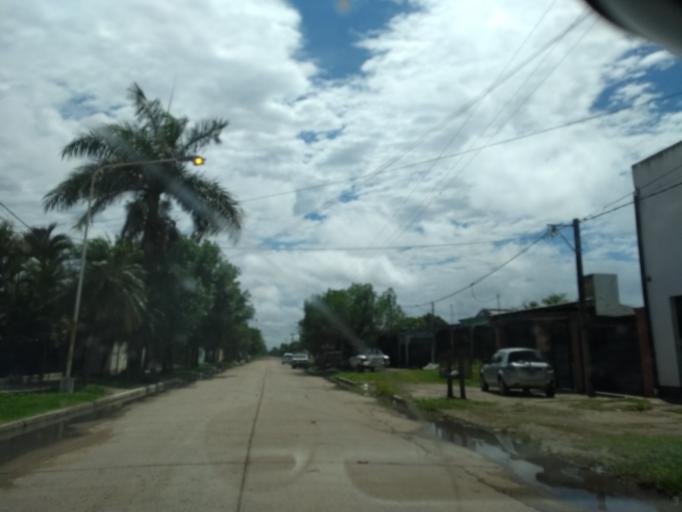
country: AR
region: Chaco
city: Barranqueras
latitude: -27.4812
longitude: -58.9487
